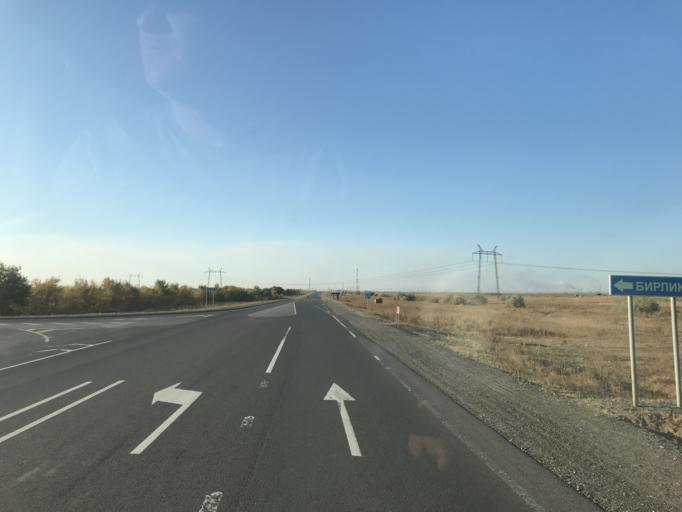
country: KZ
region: Pavlodar
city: Pavlodar
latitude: 52.0878
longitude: 77.1265
